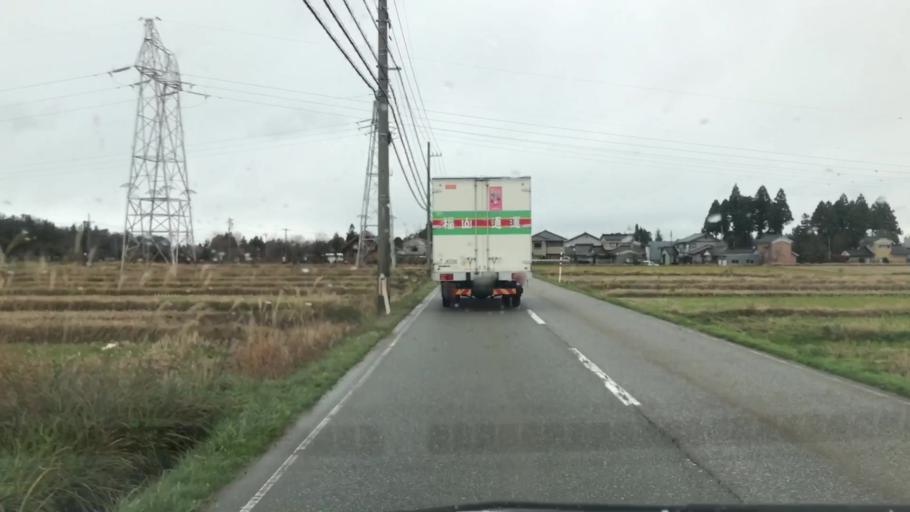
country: JP
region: Toyama
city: Kamiichi
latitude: 36.5984
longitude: 137.3238
